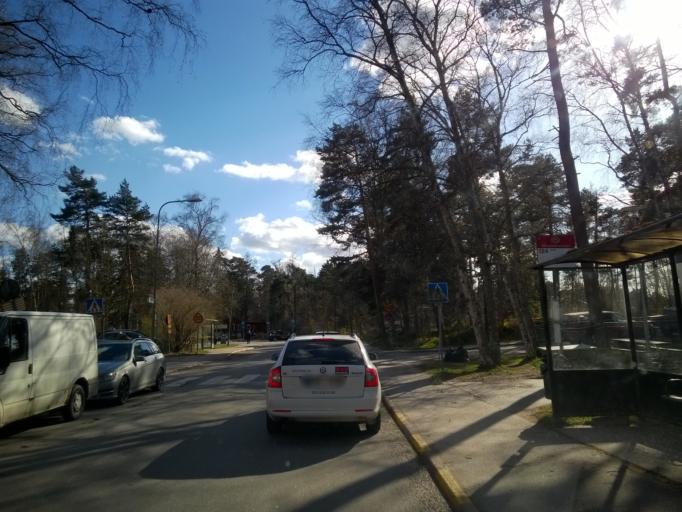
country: SE
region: Stockholm
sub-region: Stockholms Kommun
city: Bromma
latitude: 59.3297
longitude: 17.9459
